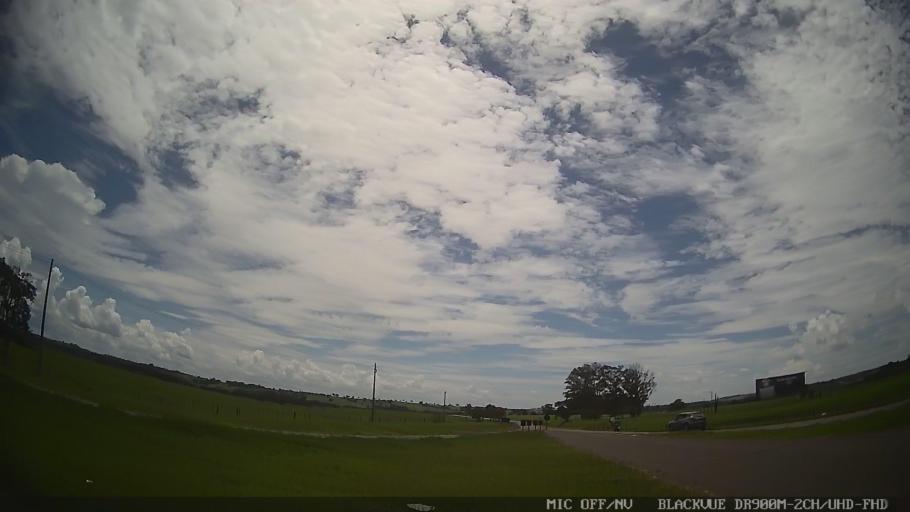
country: BR
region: Sao Paulo
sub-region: Conchas
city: Conchas
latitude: -23.0452
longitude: -47.9598
